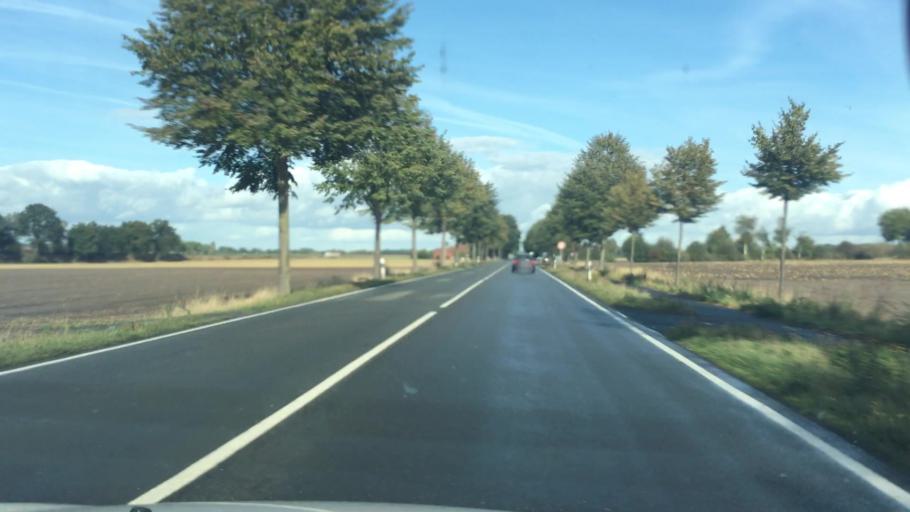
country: DE
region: Lower Saxony
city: Varrel
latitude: 52.6568
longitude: 8.7653
